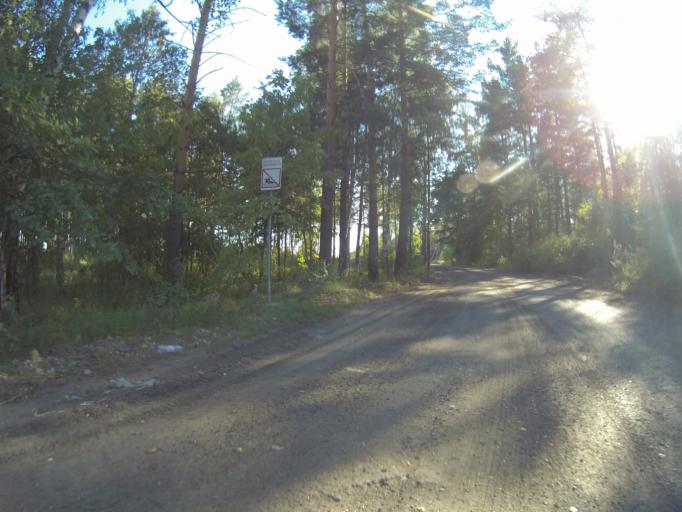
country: RU
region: Vladimir
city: Kommunar
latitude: 56.0532
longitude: 40.4154
